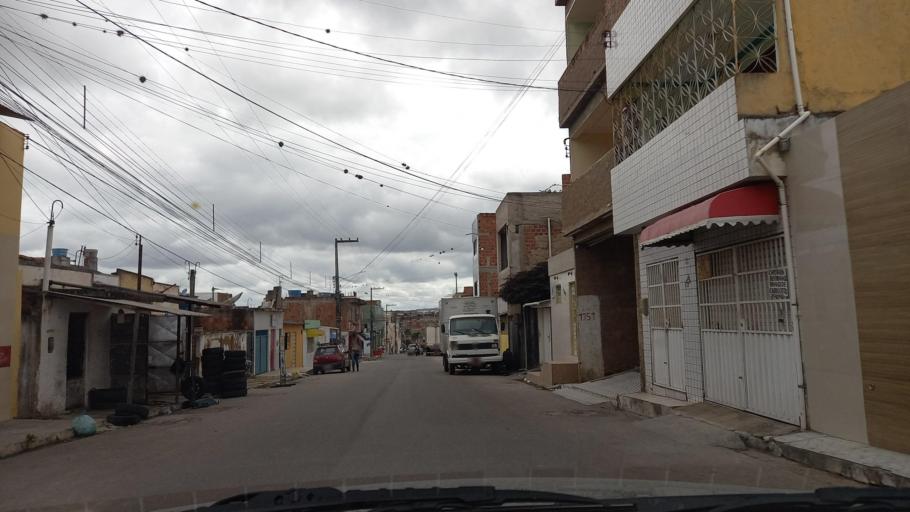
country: BR
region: Pernambuco
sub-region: Caruaru
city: Caruaru
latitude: -8.2731
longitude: -35.9558
